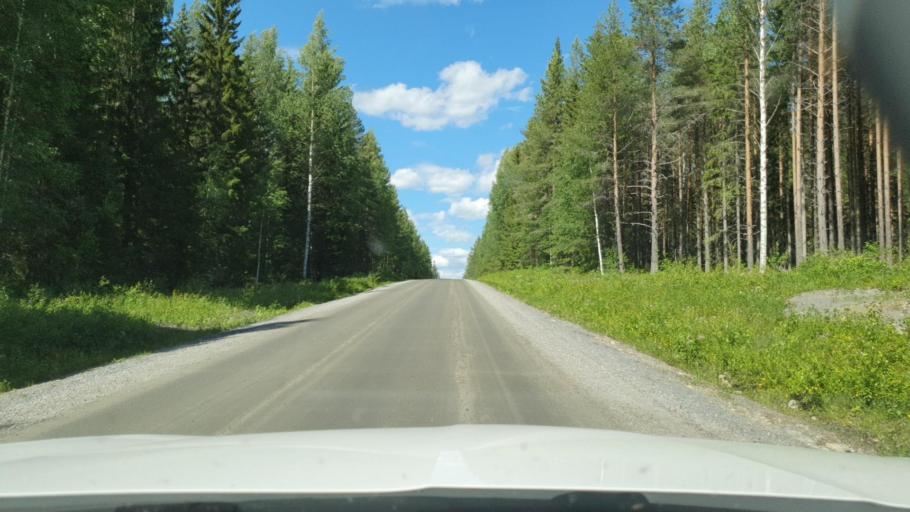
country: SE
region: Vaesterbotten
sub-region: Skelleftea Kommun
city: Forsbacka
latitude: 64.7970
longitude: 20.5056
